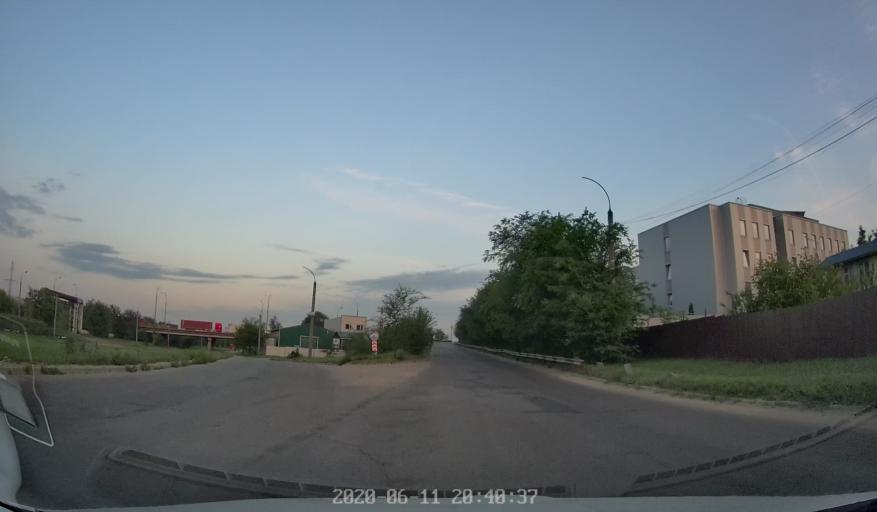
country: MD
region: Chisinau
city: Chisinau
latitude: 46.9853
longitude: 28.9028
